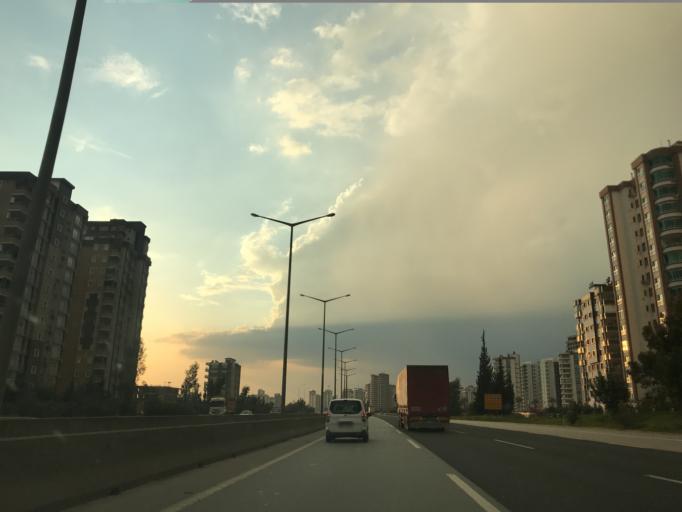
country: TR
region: Adana
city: Seyhan
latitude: 37.0322
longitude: 35.2589
